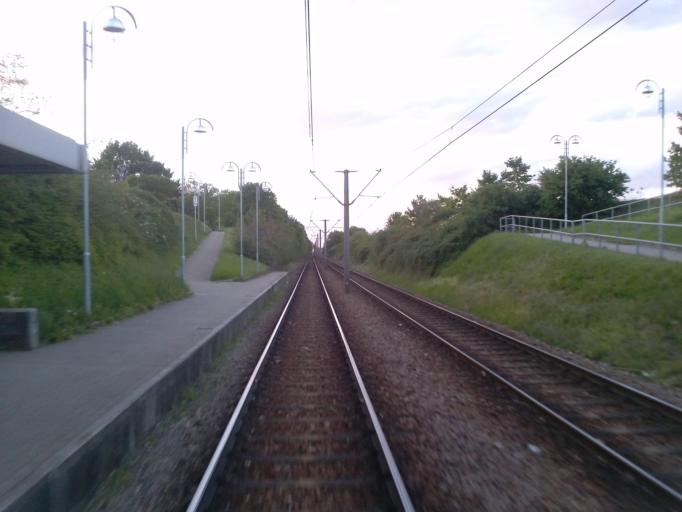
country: DE
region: Baden-Wuerttemberg
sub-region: Karlsruhe Region
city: Karlsruhe
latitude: 49.0242
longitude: 8.3757
